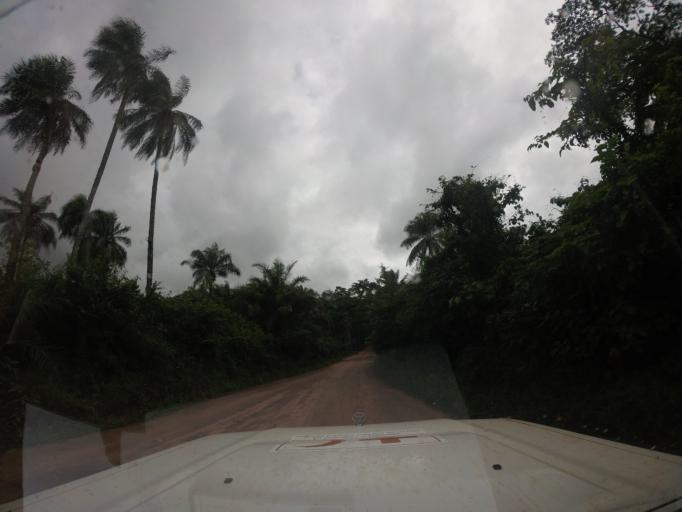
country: SL
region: Northern Province
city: Kukuna
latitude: 9.2771
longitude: -12.6738
